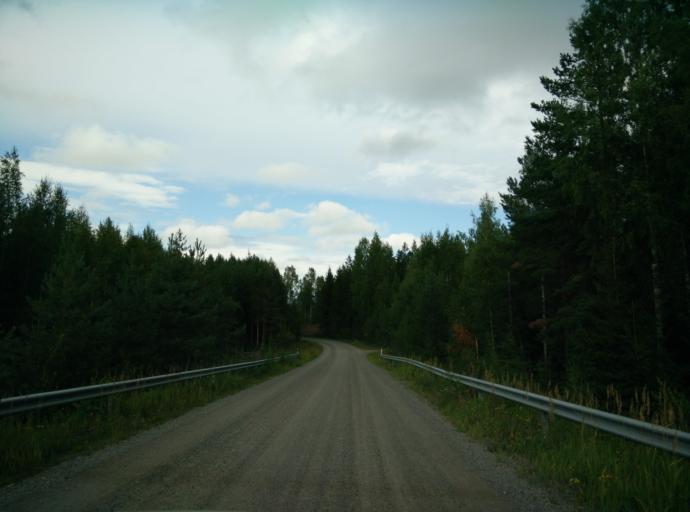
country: FI
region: Haeme
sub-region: Haemeenlinna
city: Kalvola
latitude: 61.1148
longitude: 24.1372
